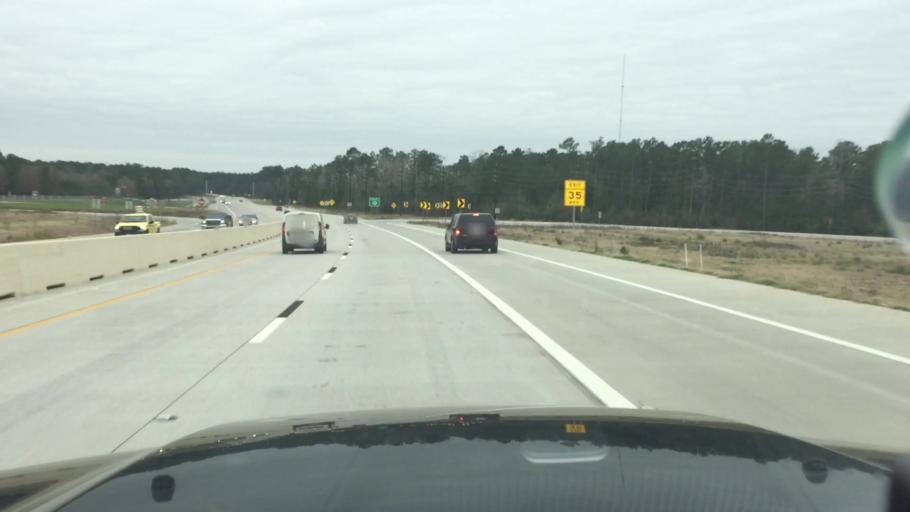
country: US
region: Texas
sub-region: Montgomery County
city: Magnolia
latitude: 30.2293
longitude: -95.6959
